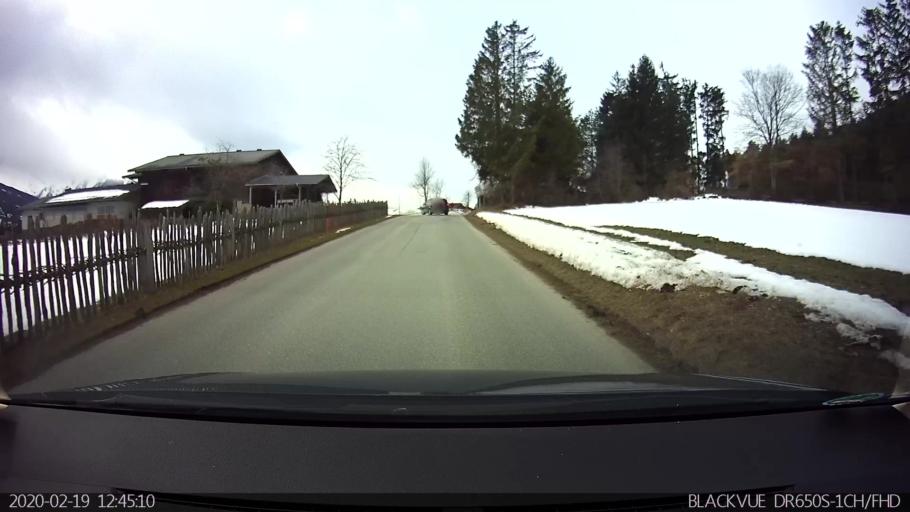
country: AT
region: Tyrol
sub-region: Politischer Bezirk Innsbruck Land
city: Fritzens
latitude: 47.3238
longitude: 11.5921
